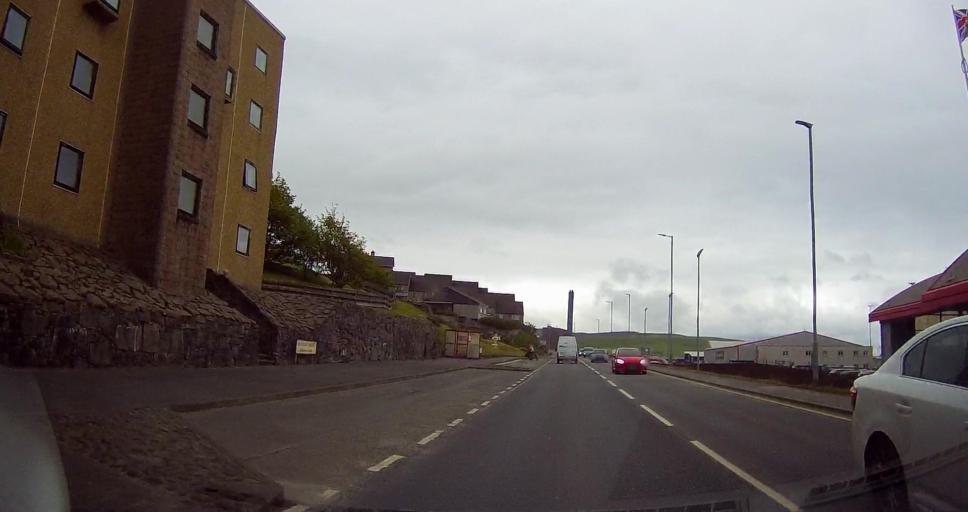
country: GB
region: Scotland
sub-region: Shetland Islands
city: Lerwick
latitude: 60.1622
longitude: -1.1589
